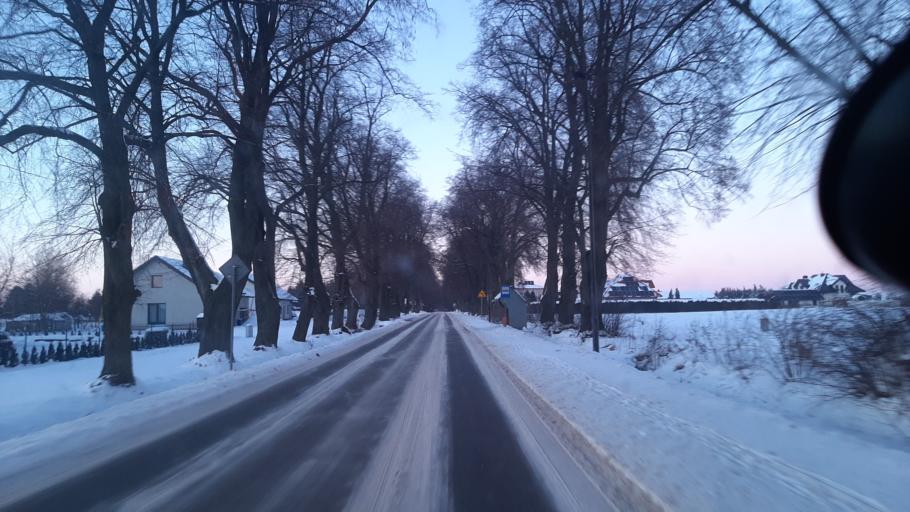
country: PL
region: Lublin Voivodeship
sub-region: Powiat lubelski
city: Lublin
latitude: 51.3221
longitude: 22.5610
